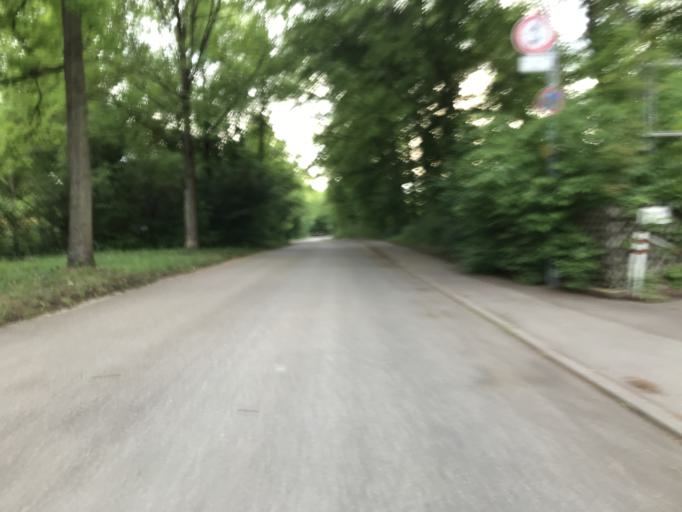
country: DE
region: Baden-Wuerttemberg
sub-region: Regierungsbezirk Stuttgart
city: Stuttgart Feuerbach
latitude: 48.8293
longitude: 9.1514
